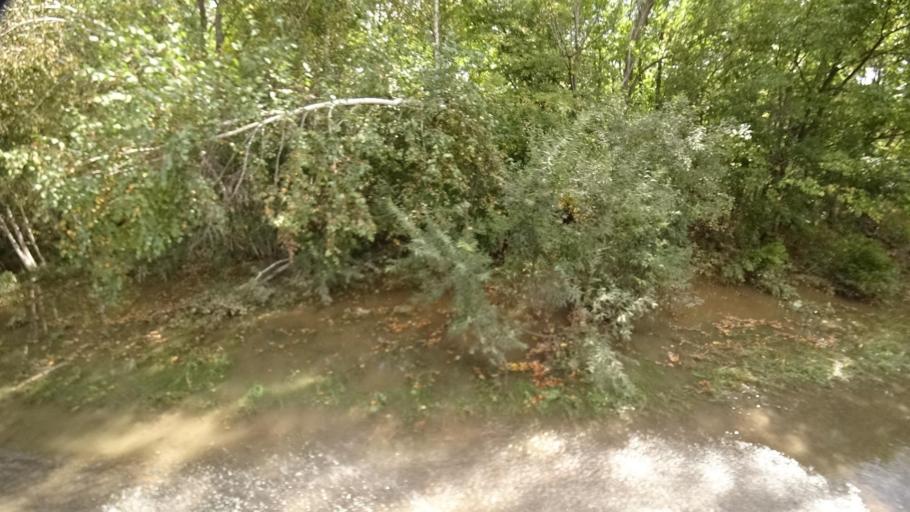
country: RU
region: Primorskiy
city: Yakovlevka
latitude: 44.6641
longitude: 133.7507
